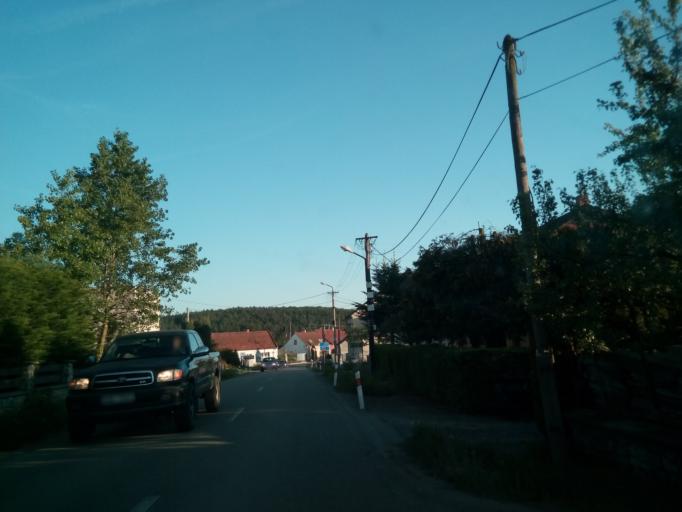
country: CZ
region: South Moravian
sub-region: Okres Blansko
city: Jedovnice
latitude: 49.2831
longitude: 16.7496
